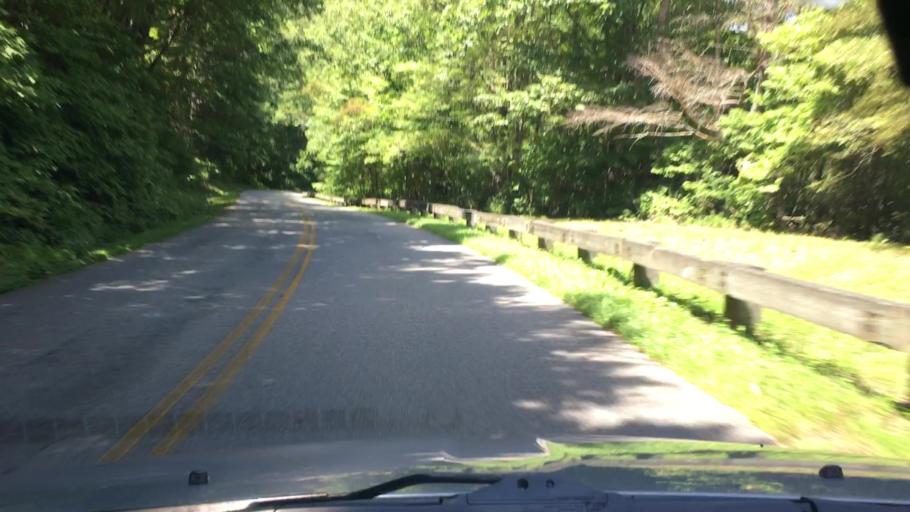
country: US
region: North Carolina
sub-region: Buncombe County
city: Asheville
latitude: 35.6394
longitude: -82.4910
